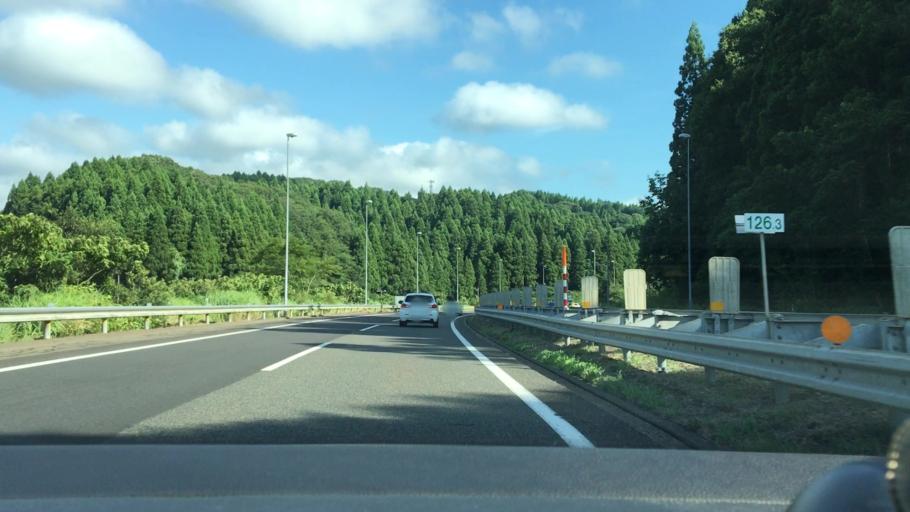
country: JP
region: Fukui
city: Maruoka
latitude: 36.2807
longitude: 136.2794
